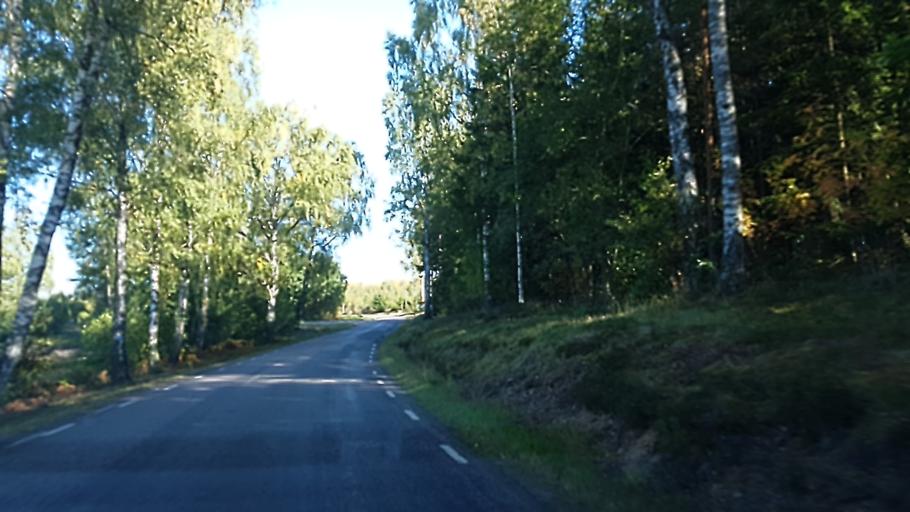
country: SE
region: Kronoberg
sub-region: Ljungby Kommun
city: Ljungby
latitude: 56.8027
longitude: 14.0333
